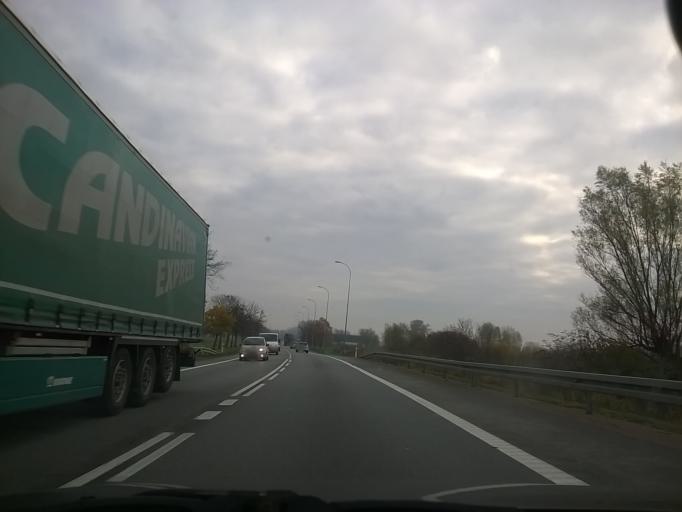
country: PL
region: Pomeranian Voivodeship
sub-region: Powiat nowodworski
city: Nowy Dwor Gdanski
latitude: 54.1885
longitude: 19.2008
